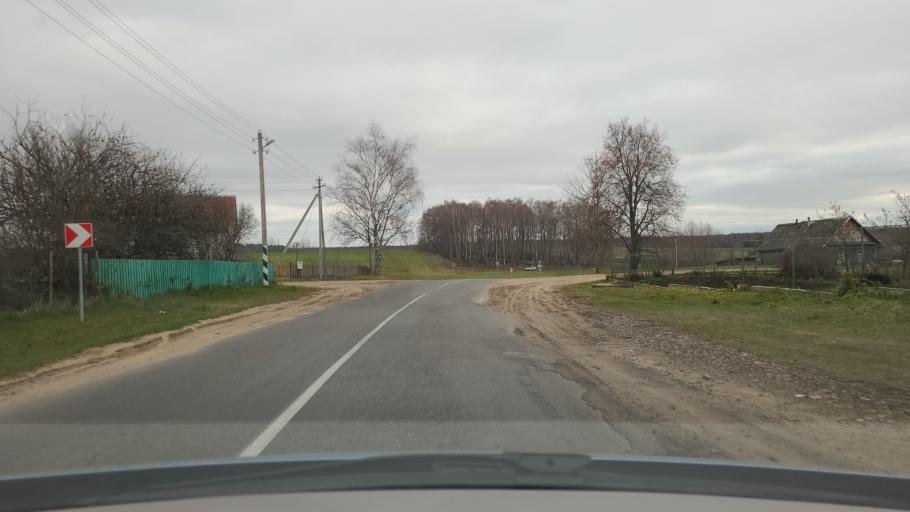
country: BY
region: Minsk
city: Khalopyenichy
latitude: 54.4693
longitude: 28.9836
